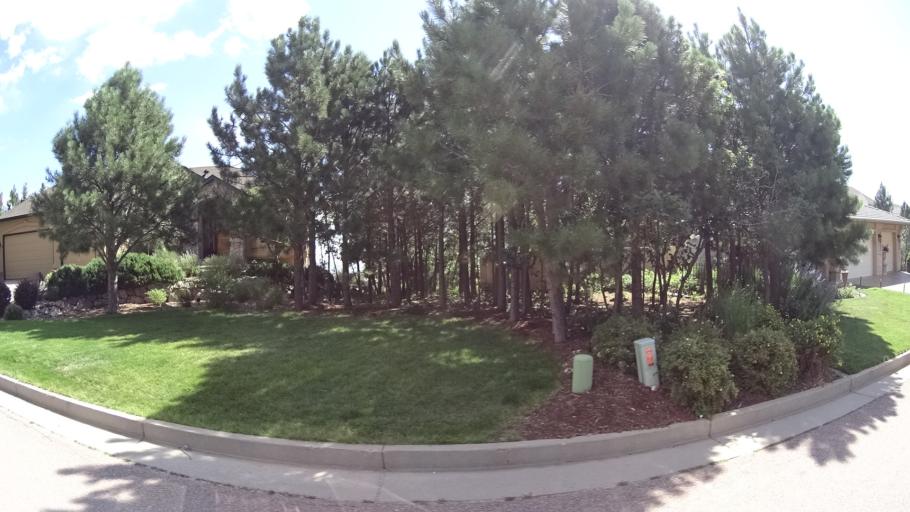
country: US
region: Colorado
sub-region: El Paso County
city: Fort Carson
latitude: 38.7421
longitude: -104.8379
